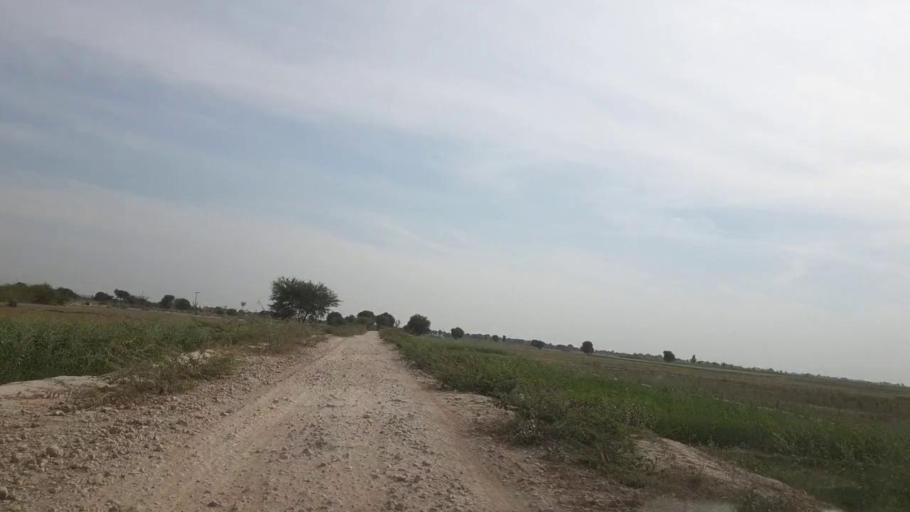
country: PK
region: Sindh
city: Nabisar
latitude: 25.0417
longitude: 69.5616
